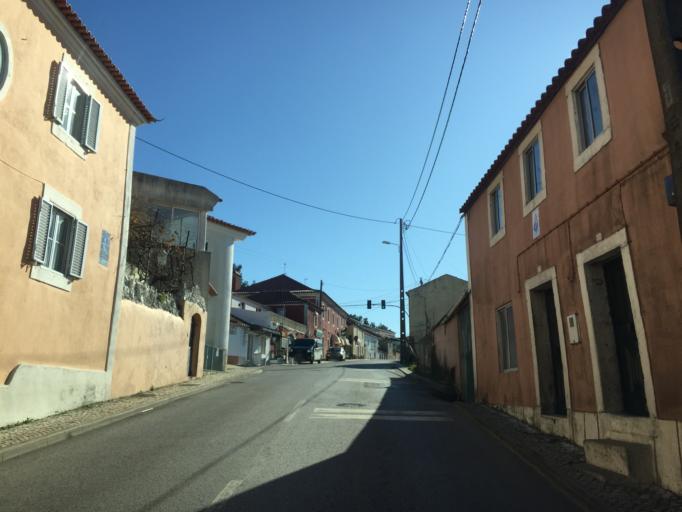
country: PT
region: Lisbon
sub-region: Sintra
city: Almargem
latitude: 38.8245
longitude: -9.2944
